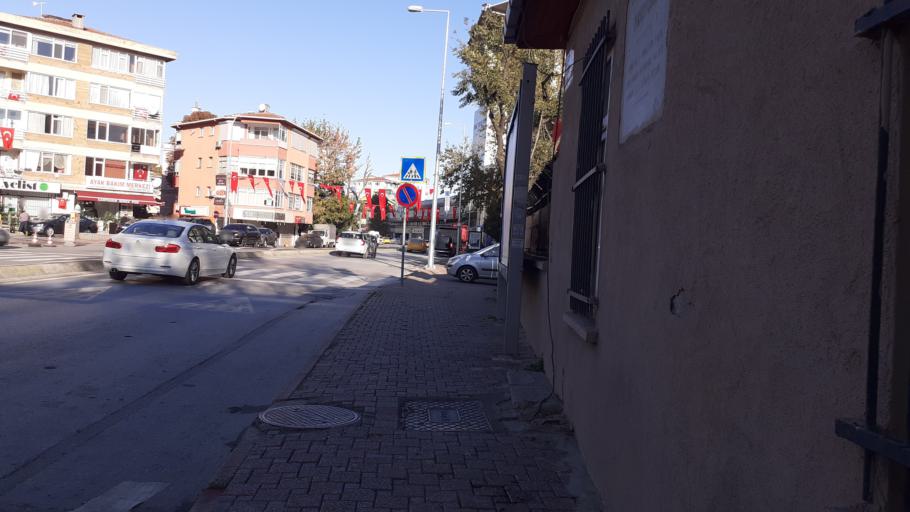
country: TR
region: Istanbul
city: UEskuedar
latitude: 40.9860
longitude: 29.0373
